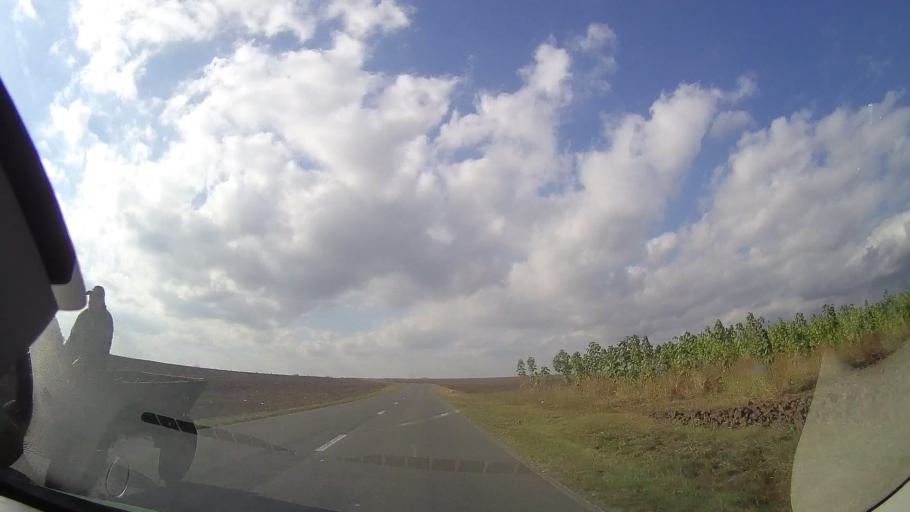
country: RO
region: Constanta
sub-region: Comuna Douazeci si Trei August
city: Dulcesti
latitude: 43.9137
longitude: 28.5626
